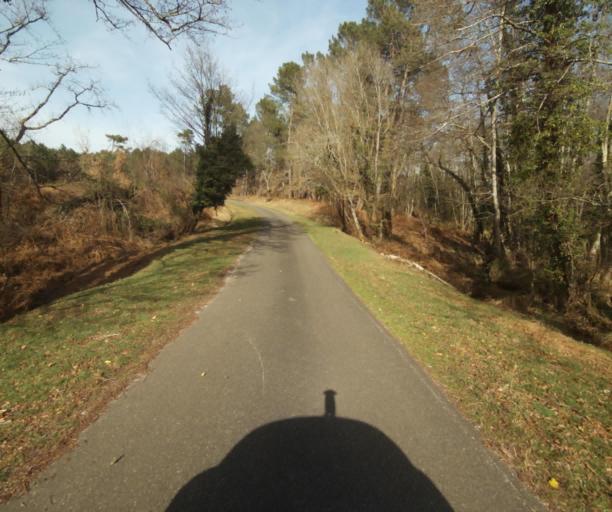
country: FR
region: Aquitaine
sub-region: Departement des Landes
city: Sarbazan
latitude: 44.1235
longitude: -0.1595
